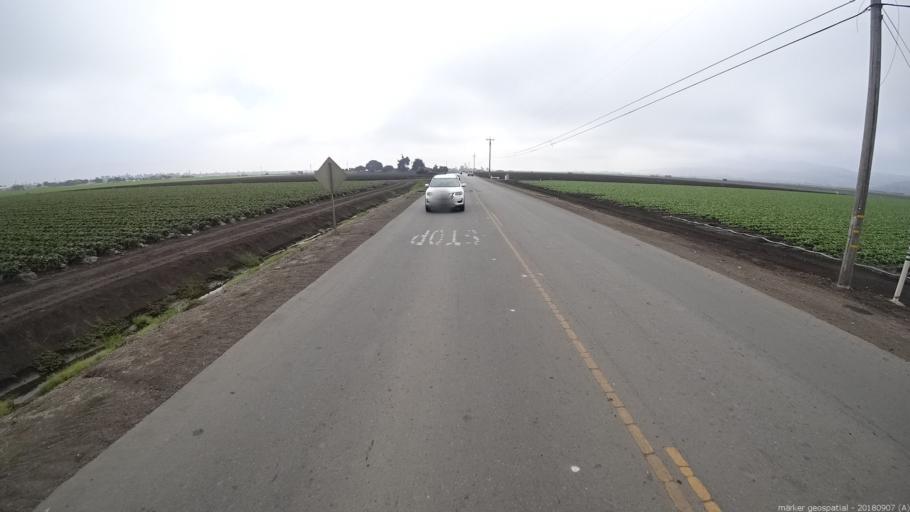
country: US
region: California
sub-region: Monterey County
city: Salinas
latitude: 36.6579
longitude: -121.6903
